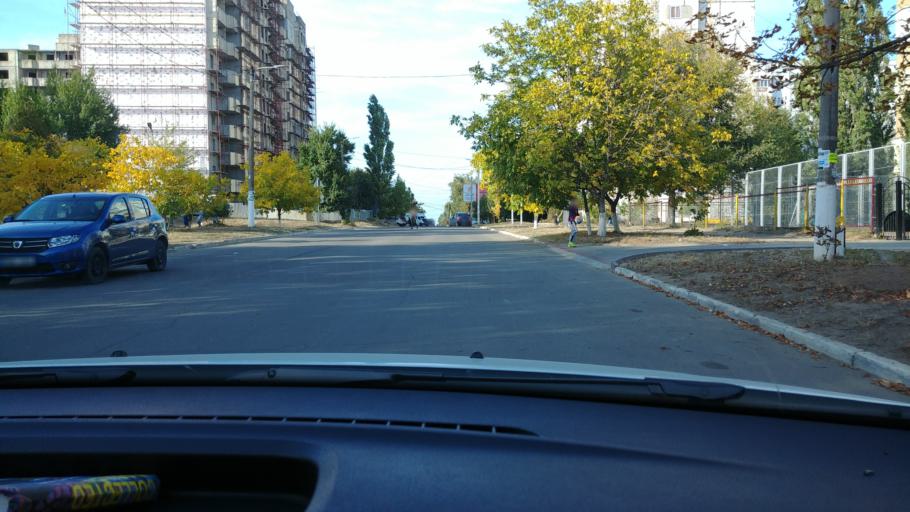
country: MD
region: Rezina
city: Rezina
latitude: 47.7473
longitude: 28.9561
